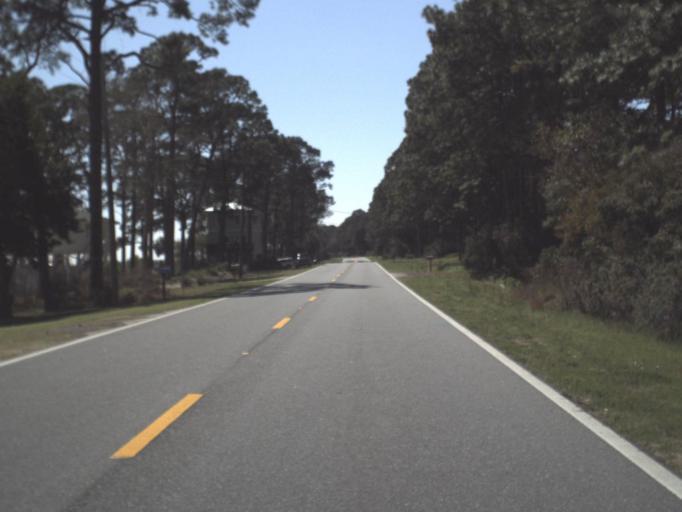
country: US
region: Florida
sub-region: Franklin County
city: Carrabelle
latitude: 29.9076
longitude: -84.5413
